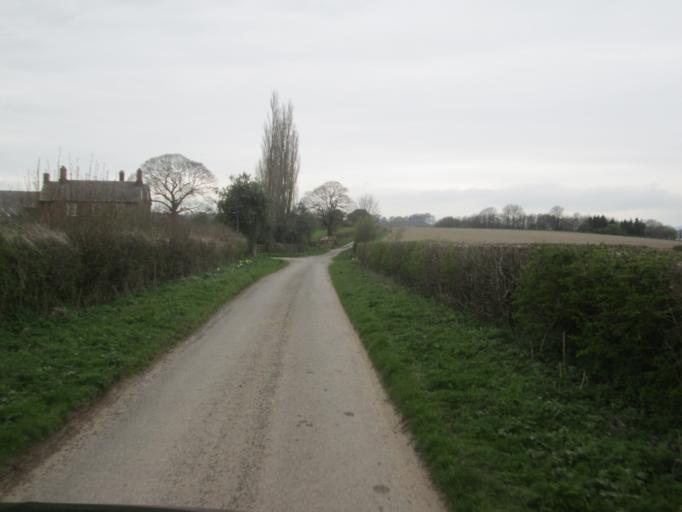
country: GB
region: England
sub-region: Derbyshire
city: Duffield
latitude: 52.9813
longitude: -1.5268
